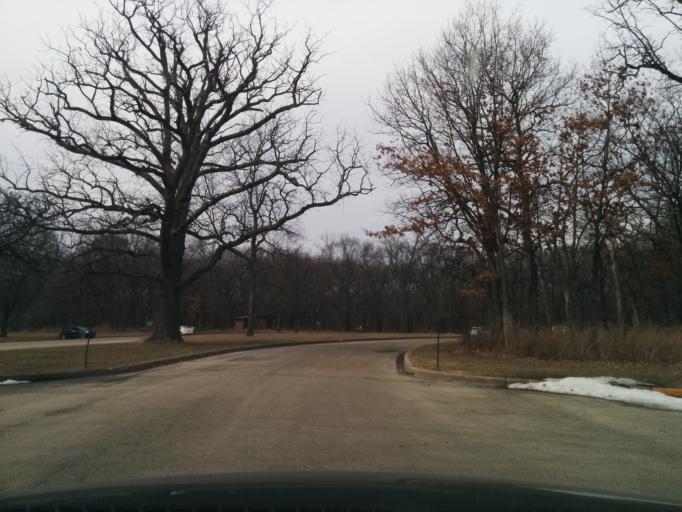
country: US
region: Illinois
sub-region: Cook County
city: Western Springs
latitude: 41.8245
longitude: -87.9085
